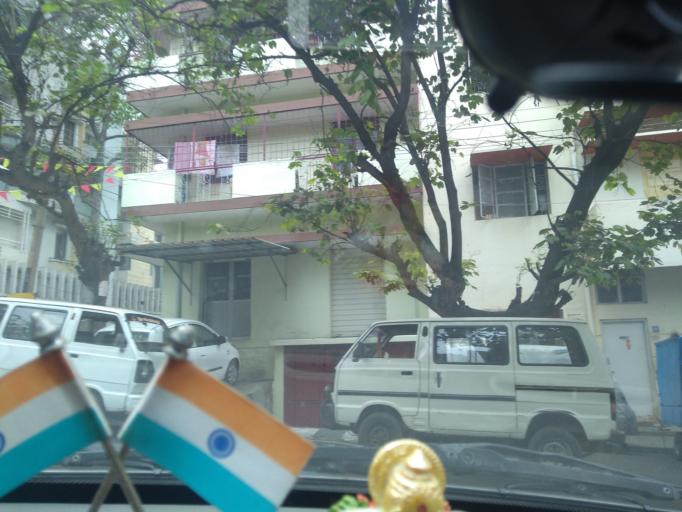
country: IN
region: Karnataka
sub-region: Bangalore Urban
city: Bangalore
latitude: 13.0050
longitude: 77.5504
